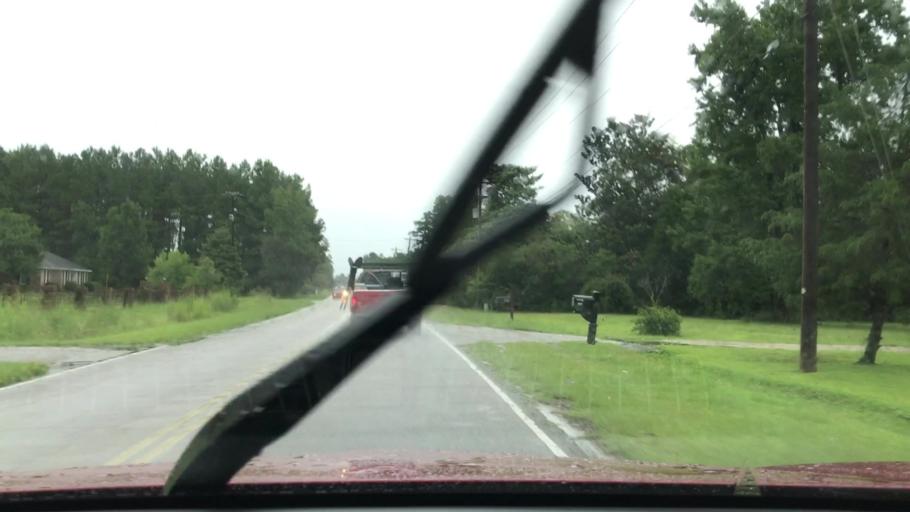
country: US
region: South Carolina
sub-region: Horry County
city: Conway
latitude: 33.8413
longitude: -79.0306
